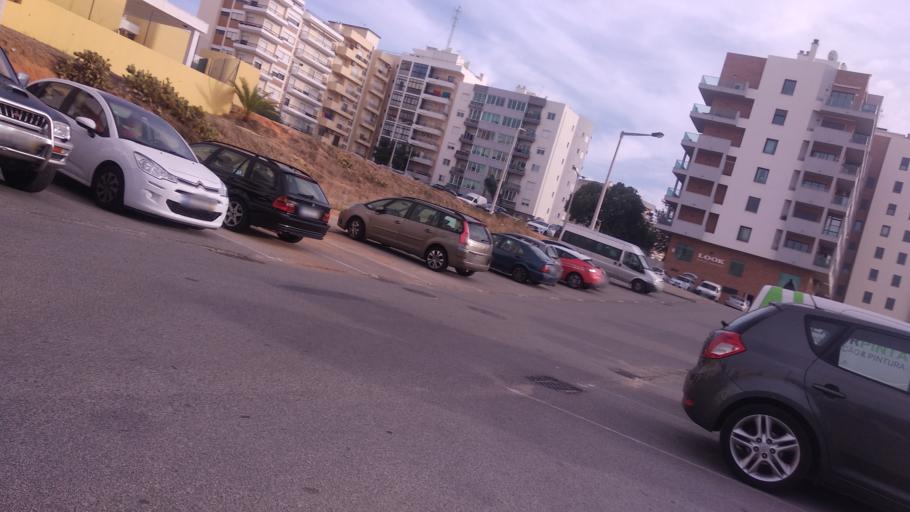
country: PT
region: Faro
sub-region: Faro
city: Faro
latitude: 37.0269
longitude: -7.9371
